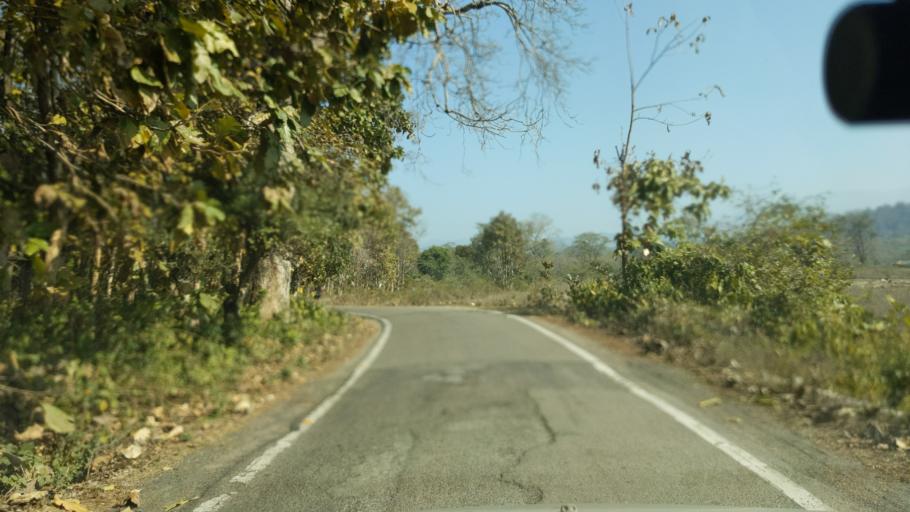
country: IN
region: Uttarakhand
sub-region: Naini Tal
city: Ramnagar
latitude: 29.4175
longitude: 79.1374
